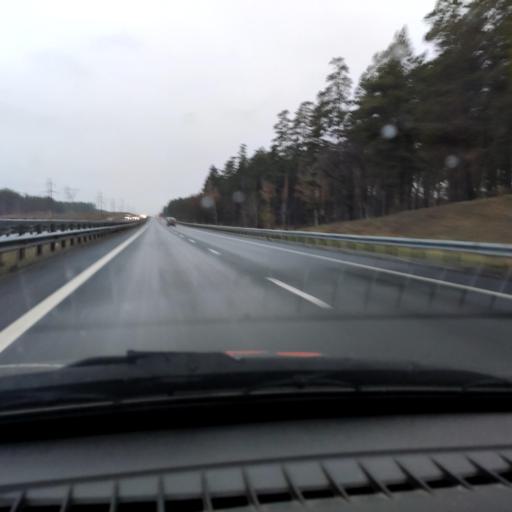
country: RU
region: Samara
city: Povolzhskiy
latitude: 53.5175
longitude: 49.7687
